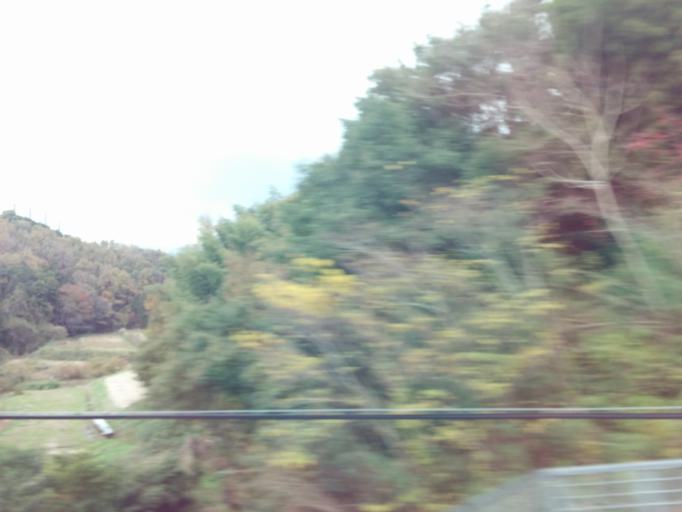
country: JP
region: Shizuoka
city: Mishima
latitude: 35.1215
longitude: 138.9420
